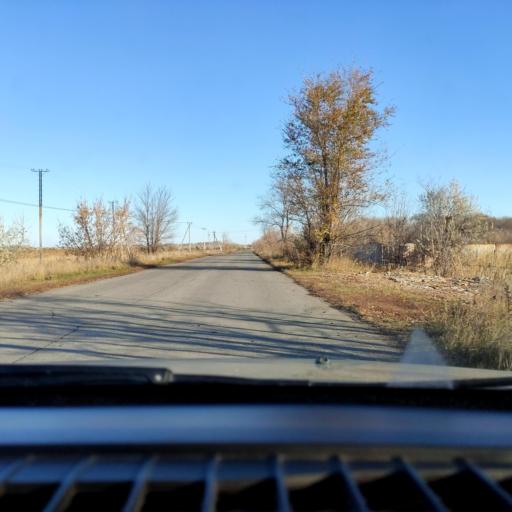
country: RU
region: Samara
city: Tol'yatti
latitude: 53.6468
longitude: 49.3192
